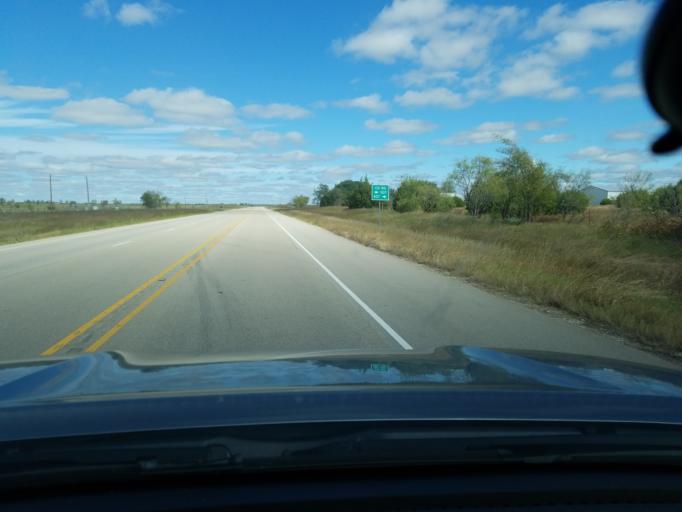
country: US
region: Texas
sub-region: Hamilton County
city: Hamilton
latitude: 31.6248
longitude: -98.1552
